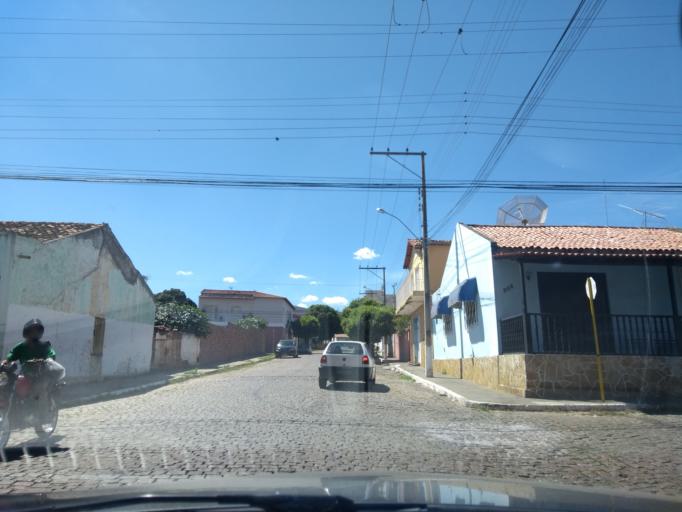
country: BR
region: Bahia
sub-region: Brumado
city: Brumado
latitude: -14.2064
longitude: -41.6676
